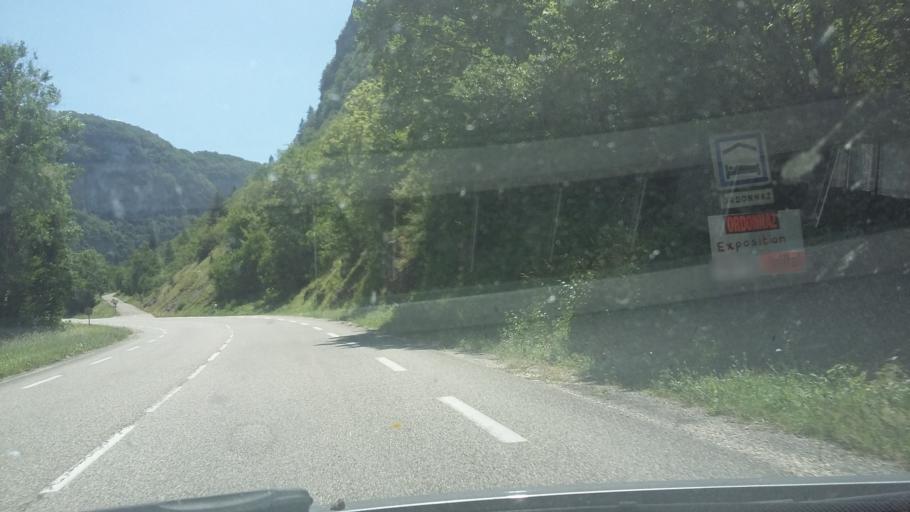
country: FR
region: Rhone-Alpes
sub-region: Departement de l'Ain
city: Tenay
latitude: 45.8889
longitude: 5.5311
